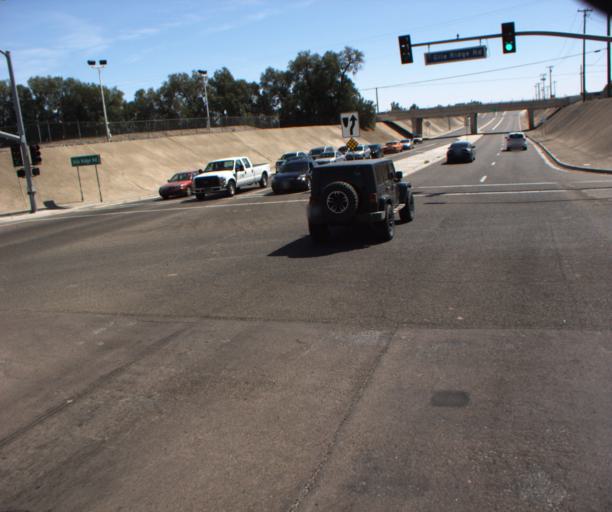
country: US
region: Arizona
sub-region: Yuma County
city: Fortuna Foothills
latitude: 32.6768
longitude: -114.5215
